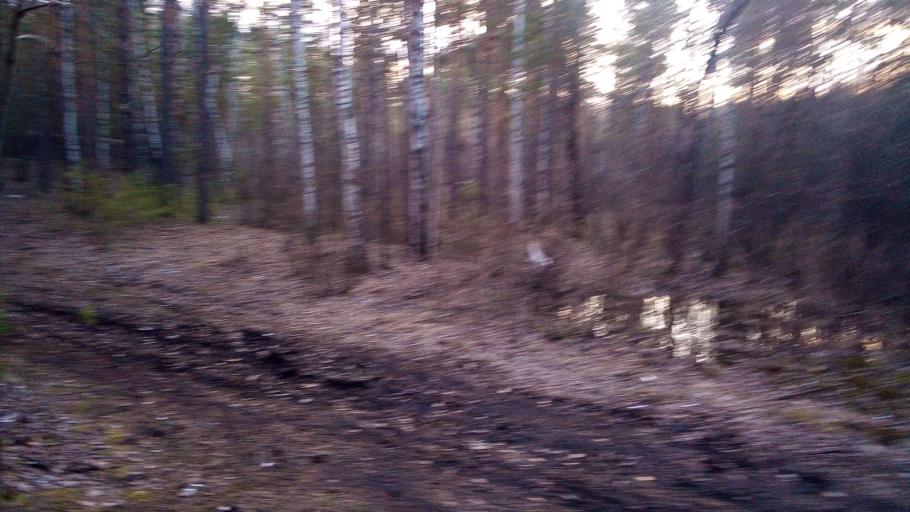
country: RU
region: Chelyabinsk
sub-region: Gorod Chelyabinsk
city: Chelyabinsk
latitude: 55.1652
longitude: 61.3262
